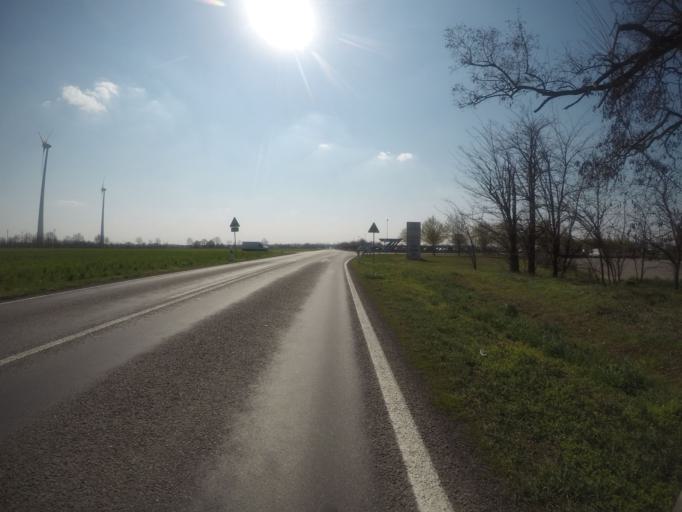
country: DE
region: Brandenburg
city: Ketzin
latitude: 52.5372
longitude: 12.8695
